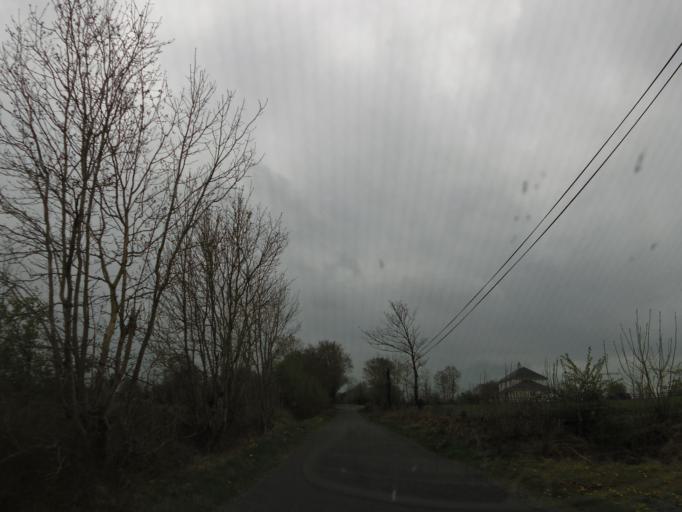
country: IE
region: Connaught
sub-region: Maigh Eo
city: Kiltamagh
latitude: 53.7897
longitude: -8.9630
